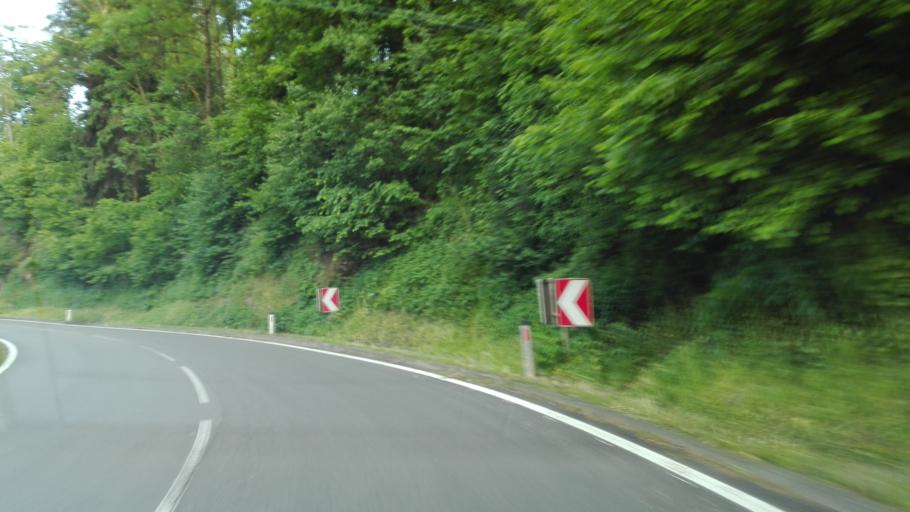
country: AT
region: Upper Austria
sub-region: Politischer Bezirk Urfahr-Umgebung
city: Engerwitzdorf
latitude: 48.3380
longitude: 14.4601
